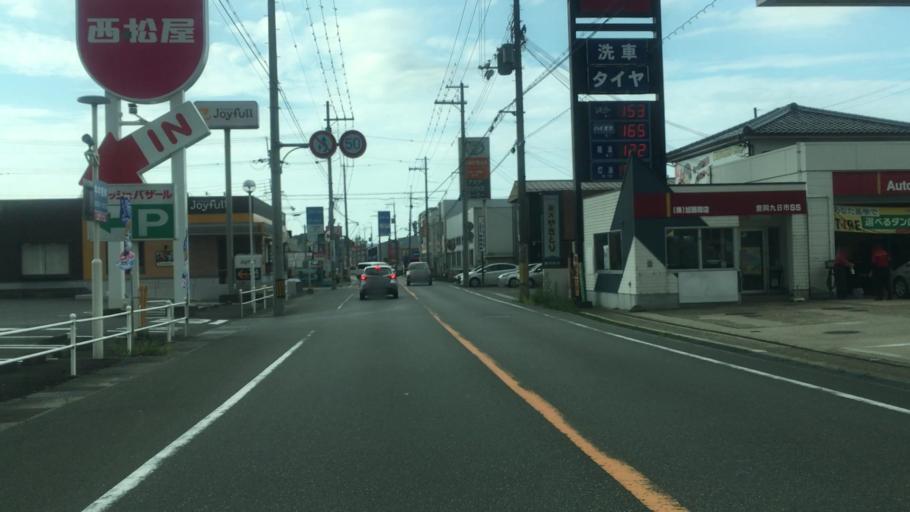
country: JP
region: Hyogo
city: Toyooka
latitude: 35.5247
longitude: 134.8213
